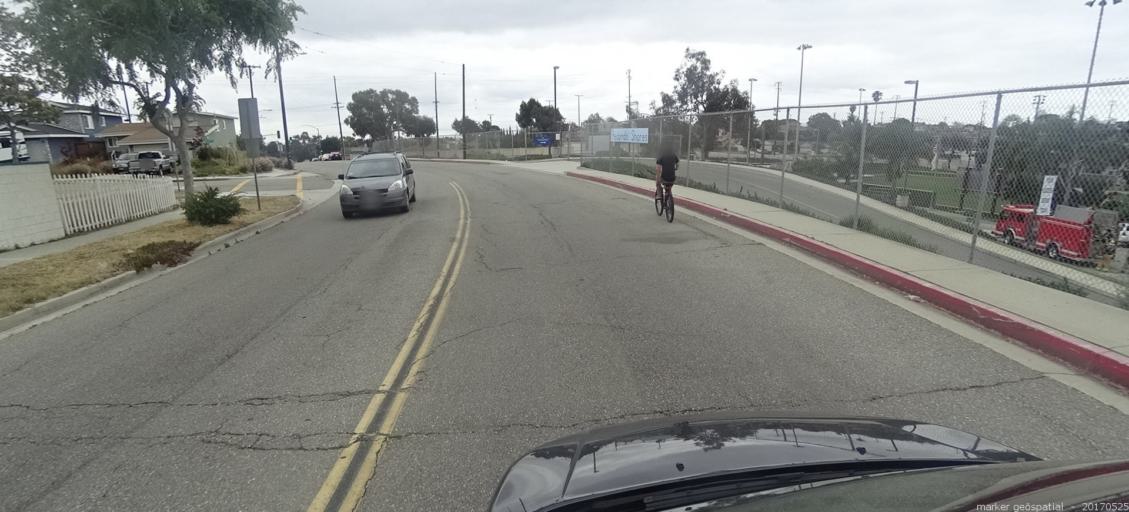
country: US
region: California
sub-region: Los Angeles County
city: Redondo Beach
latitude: 33.8480
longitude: -118.3791
